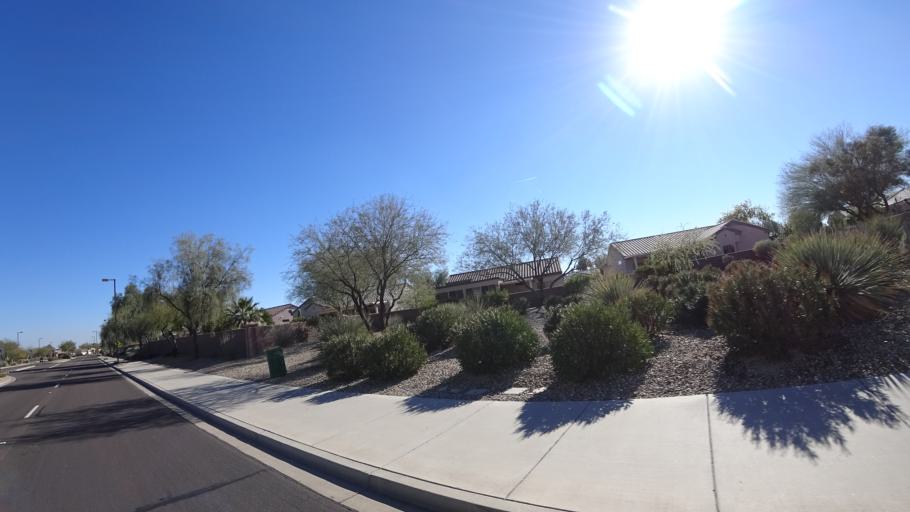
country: US
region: Arizona
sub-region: Maricopa County
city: Sun City West
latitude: 33.6528
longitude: -112.3978
